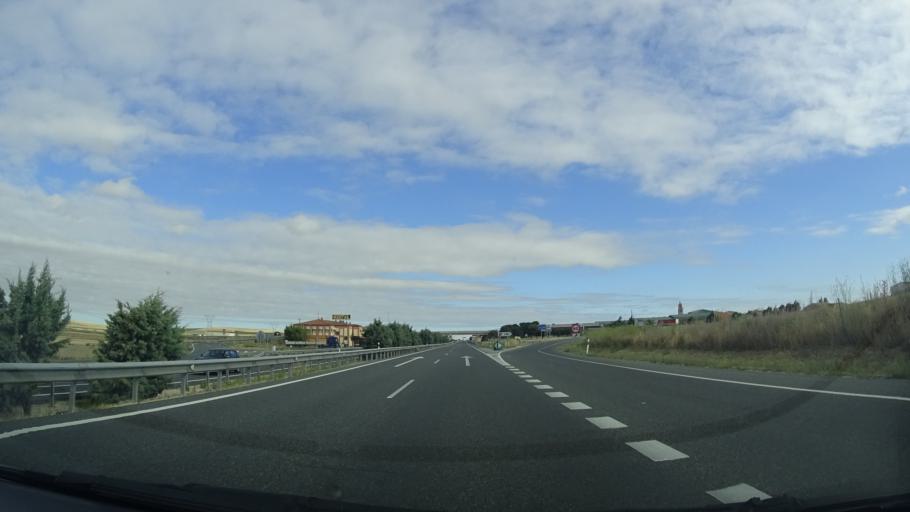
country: ES
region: Castille and Leon
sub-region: Provincia de Valladolid
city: Ataquines
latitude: 41.1744
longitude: -4.8040
